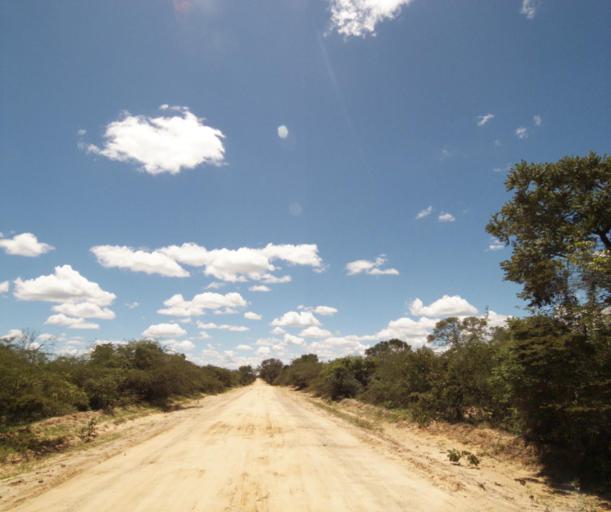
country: BR
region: Bahia
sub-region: Carinhanha
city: Carinhanha
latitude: -14.2065
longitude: -43.9558
